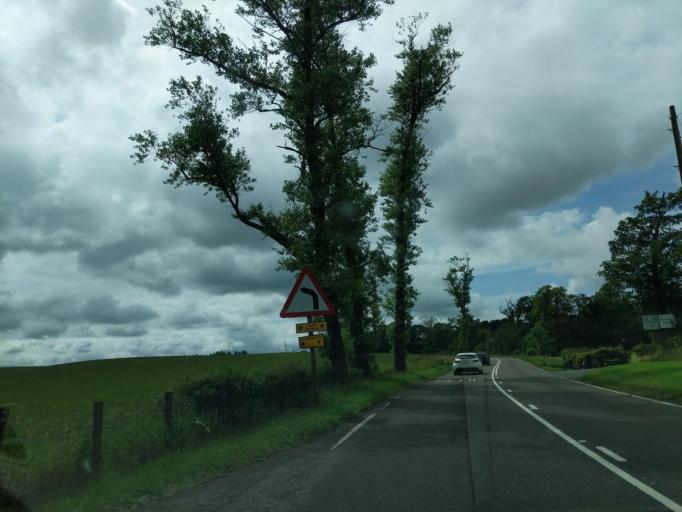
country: GB
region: Scotland
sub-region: South Lanarkshire
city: Strathaven
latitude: 55.6827
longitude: -4.0327
